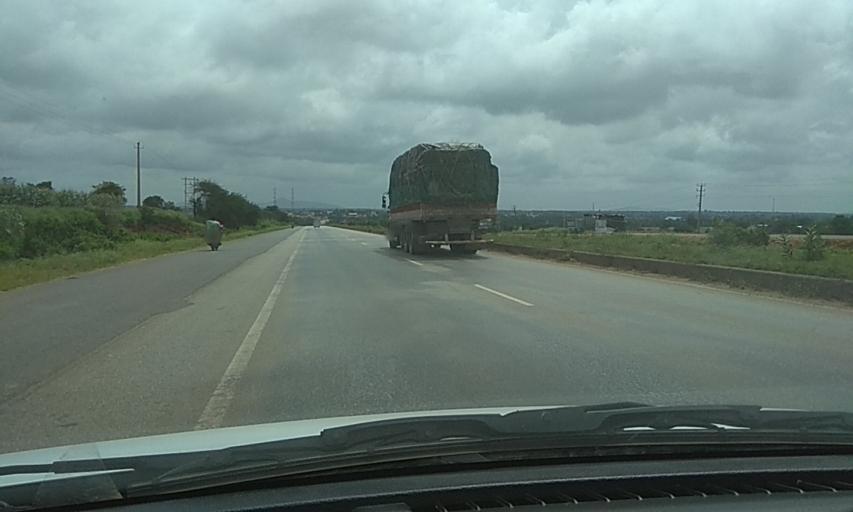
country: IN
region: Karnataka
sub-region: Davanagere
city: Mayakonda
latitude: 14.3697
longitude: 76.1751
